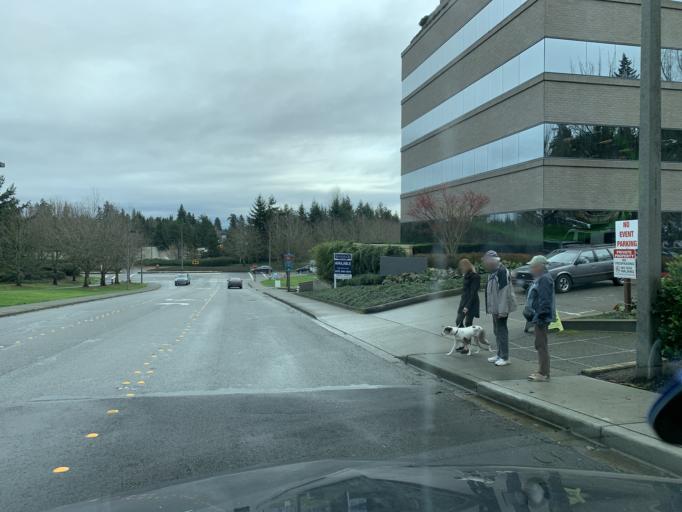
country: US
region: Washington
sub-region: King County
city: Mercer Island
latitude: 47.5891
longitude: -122.2392
